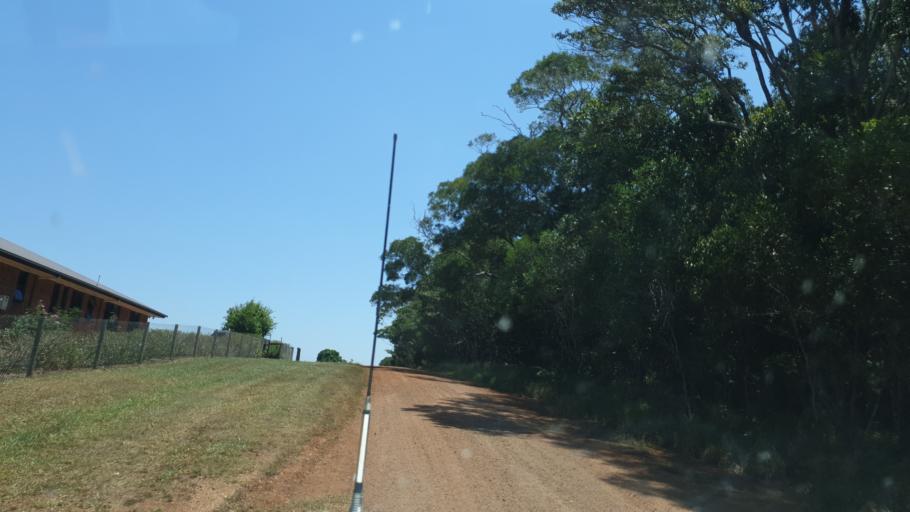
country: AU
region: Queensland
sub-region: Tablelands
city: Atherton
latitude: -17.3437
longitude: 145.6237
